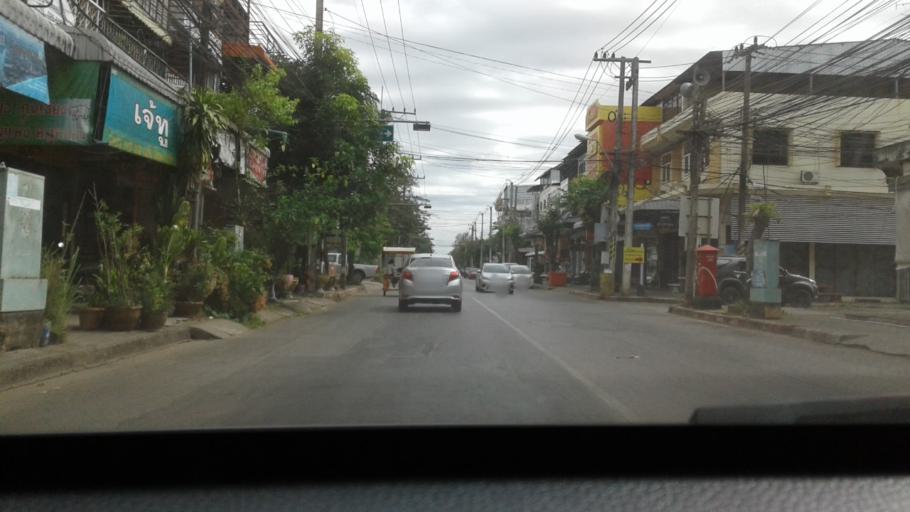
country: TH
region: Changwat Udon Thani
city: Udon Thani
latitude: 17.4113
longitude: 102.7960
